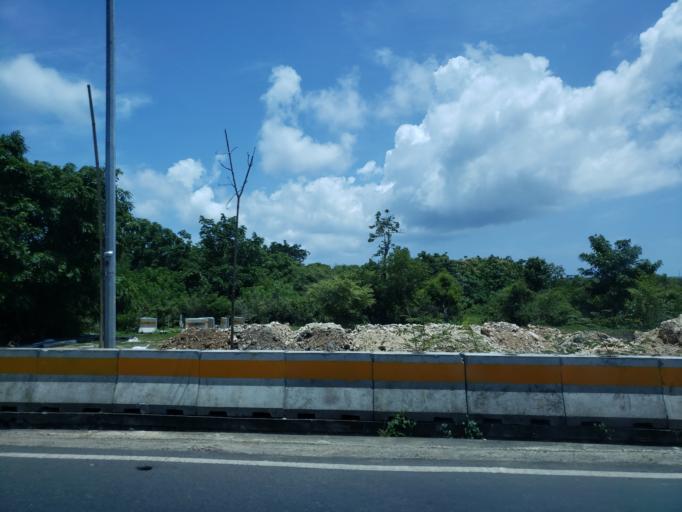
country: ID
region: Bali
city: Jimbaran
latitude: -8.7903
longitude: 115.1640
